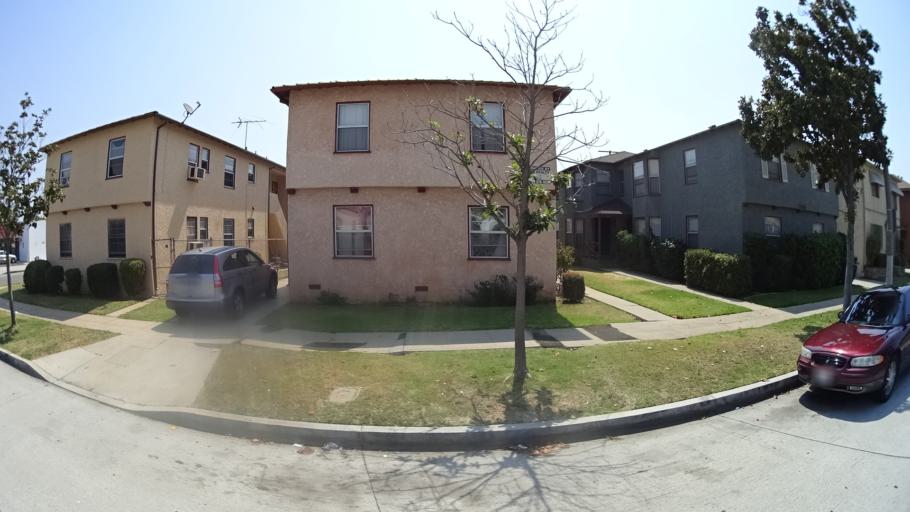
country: US
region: California
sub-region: Los Angeles County
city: Inglewood
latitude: 33.9668
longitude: -118.3308
